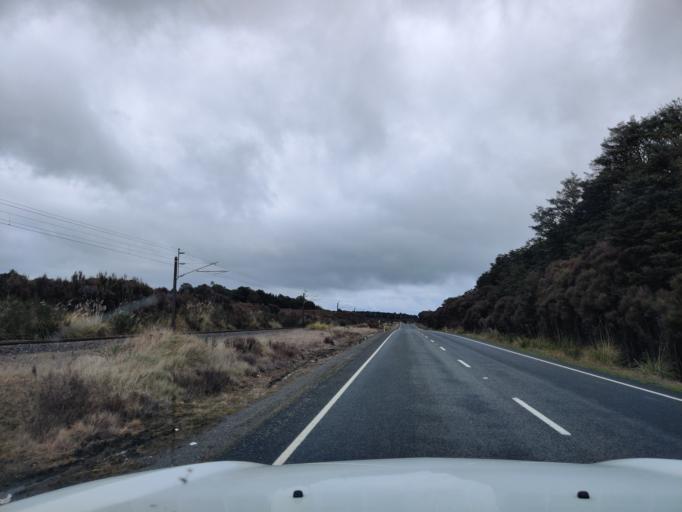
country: NZ
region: Manawatu-Wanganui
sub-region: Ruapehu District
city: Waiouru
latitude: -39.3191
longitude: 175.3865
